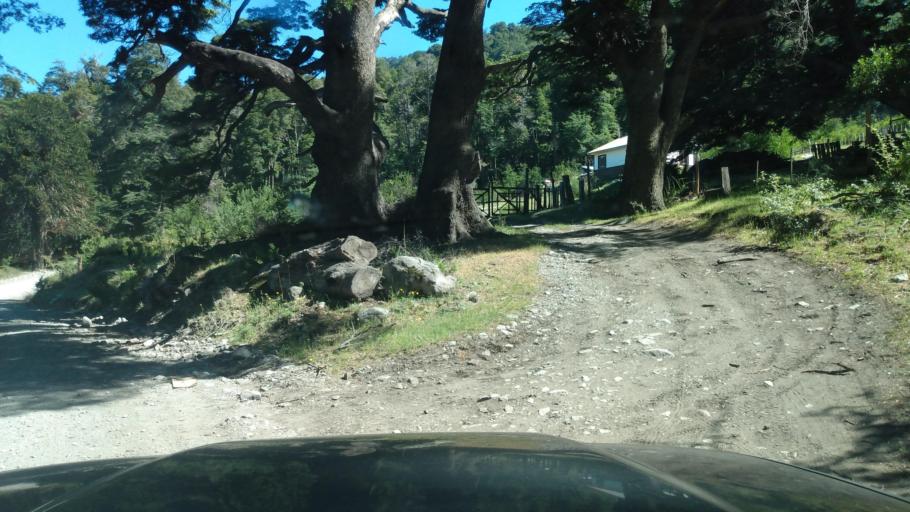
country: AR
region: Neuquen
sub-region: Departamento de Lacar
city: San Martin de los Andes
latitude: -39.7492
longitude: -71.4637
